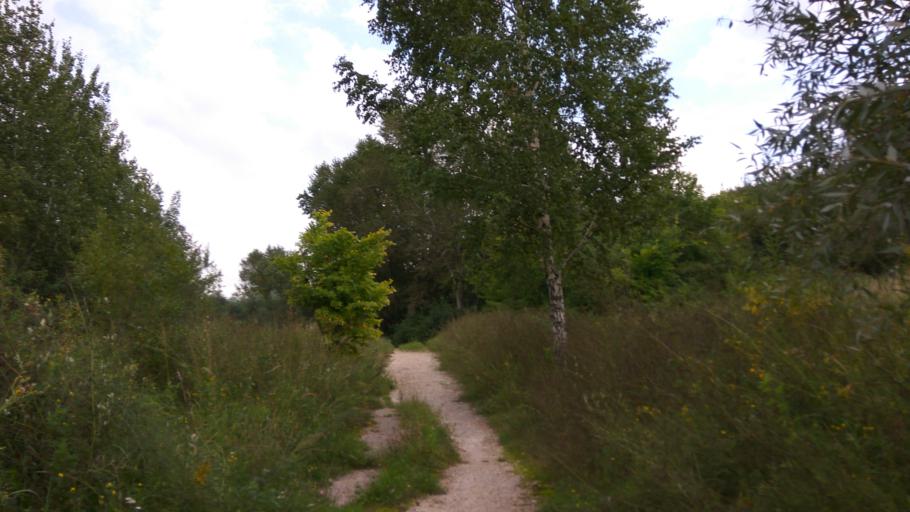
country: RU
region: Moskovskaya
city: Kur'yanovo
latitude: 55.6399
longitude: 37.7054
